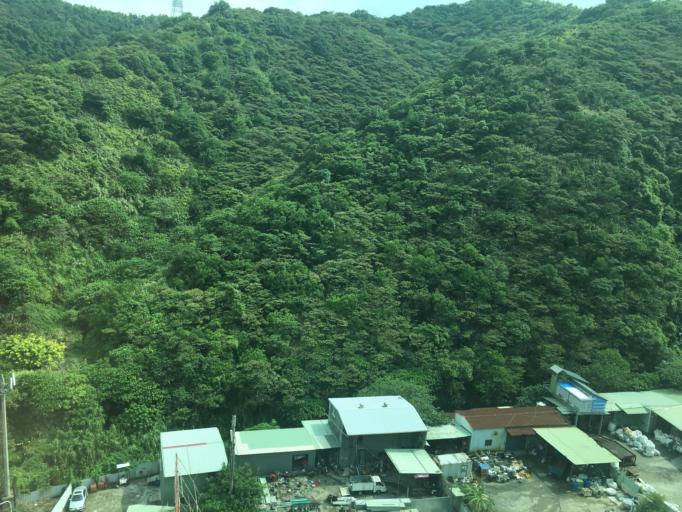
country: TW
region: Taipei
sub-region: Taipei
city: Banqiao
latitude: 25.0297
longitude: 121.4029
